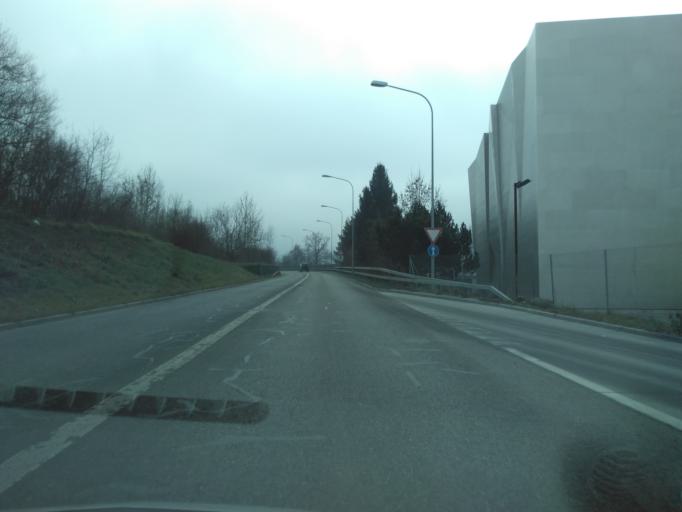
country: CH
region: Zurich
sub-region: Bezirk Zuerich
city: Zuerich (Kreis 12) / Auzelg
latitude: 47.4149
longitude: 8.5663
